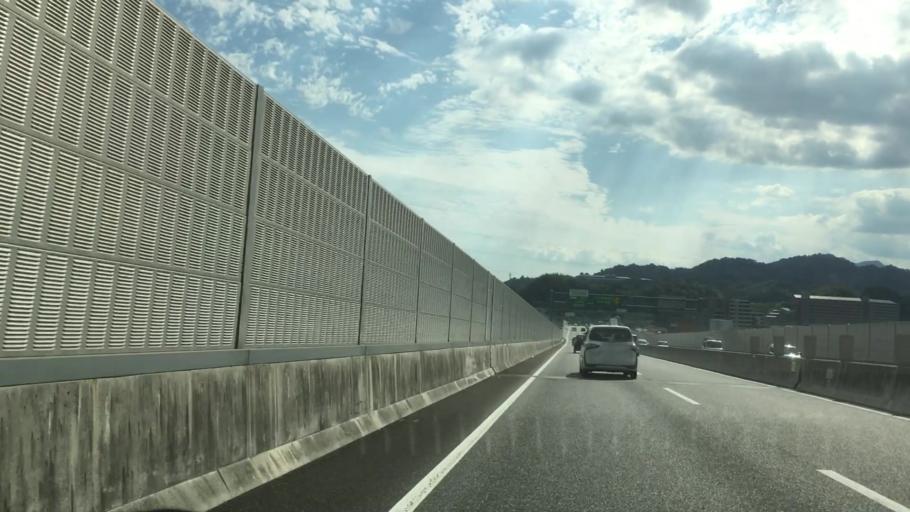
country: JP
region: Hiroshima
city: Hatsukaichi
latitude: 34.3523
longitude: 132.3209
